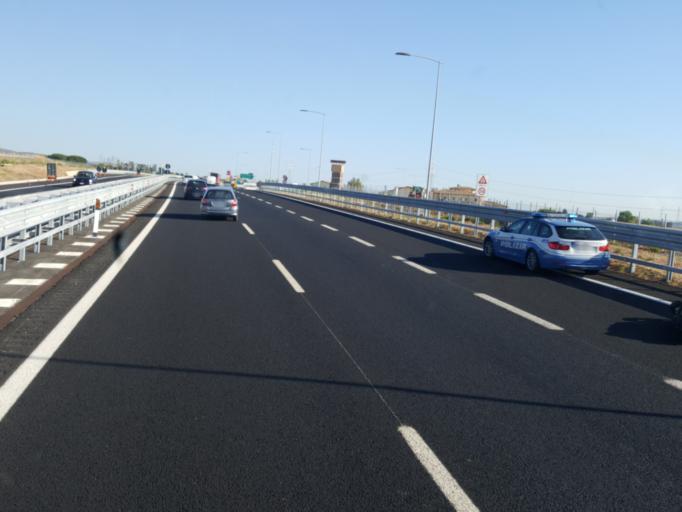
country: IT
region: Latium
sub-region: Citta metropolitana di Roma Capitale
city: Aurelia
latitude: 42.1859
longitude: 11.7875
